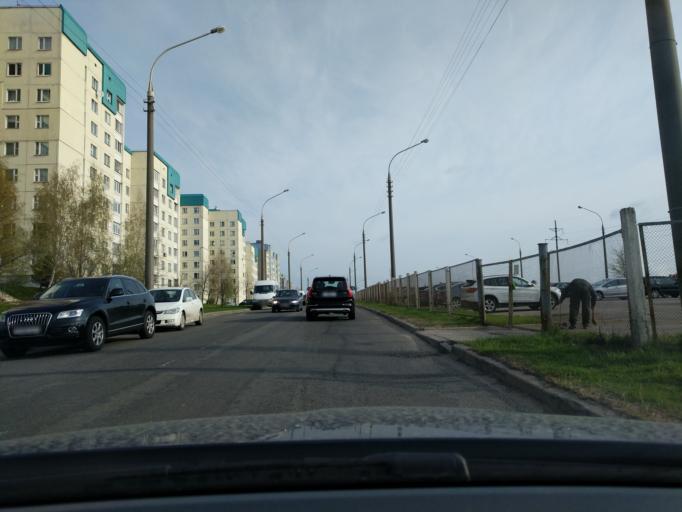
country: BY
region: Minsk
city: Novoye Medvezhino
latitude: 53.8964
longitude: 27.4631
